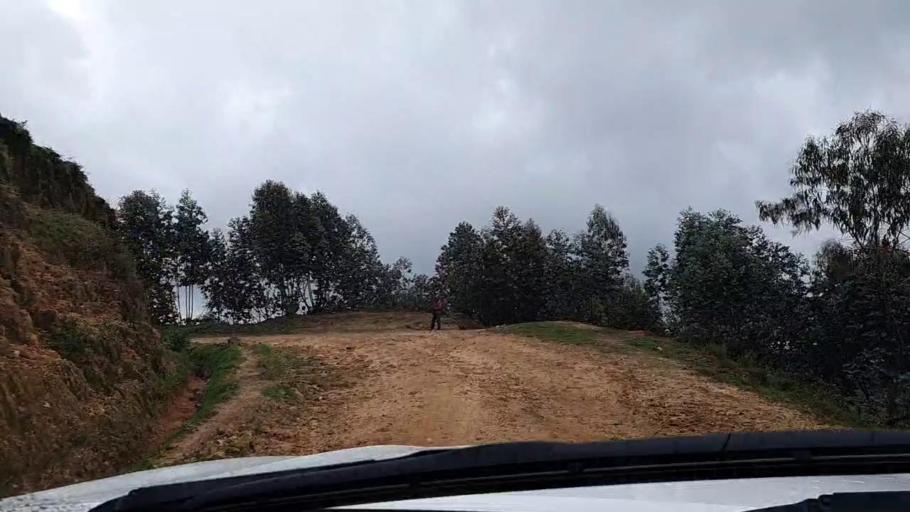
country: RW
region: Western Province
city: Kibuye
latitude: -2.2898
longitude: 29.3826
